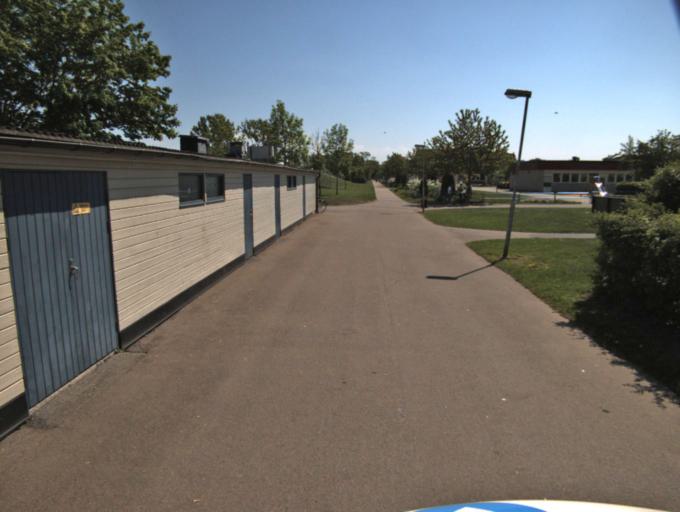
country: SE
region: Skane
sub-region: Kristianstads Kommun
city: Kristianstad
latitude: 56.0589
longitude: 14.1565
